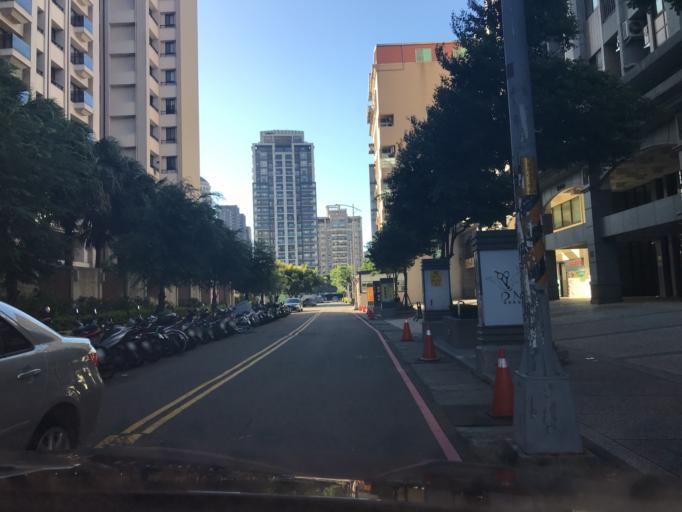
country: TW
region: Taiwan
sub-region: Hsinchu
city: Zhubei
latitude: 24.8035
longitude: 121.0332
